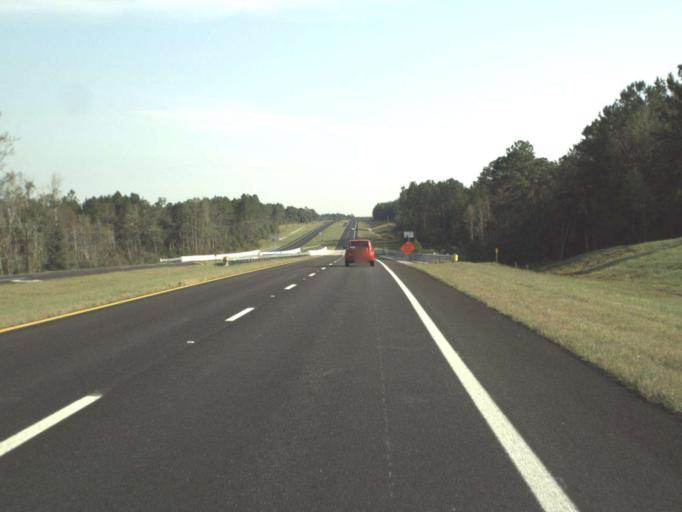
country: US
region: Florida
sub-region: Walton County
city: Freeport
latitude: 30.5266
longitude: -85.8388
